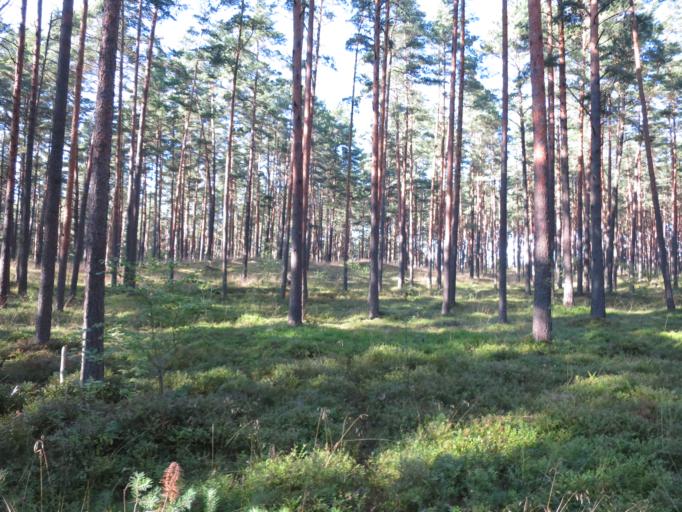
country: LV
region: Riga
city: Jaunciems
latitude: 57.0778
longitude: 24.2000
